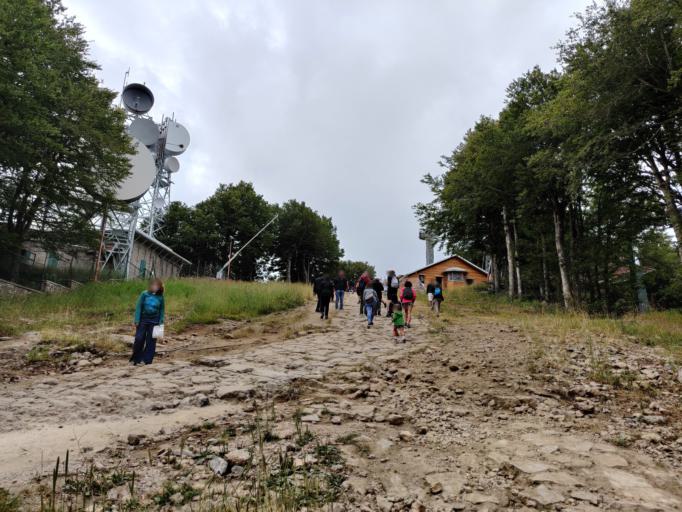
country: IT
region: Tuscany
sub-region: Provincia di Siena
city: Abbadia San Salvatore
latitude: 42.8889
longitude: 11.6255
